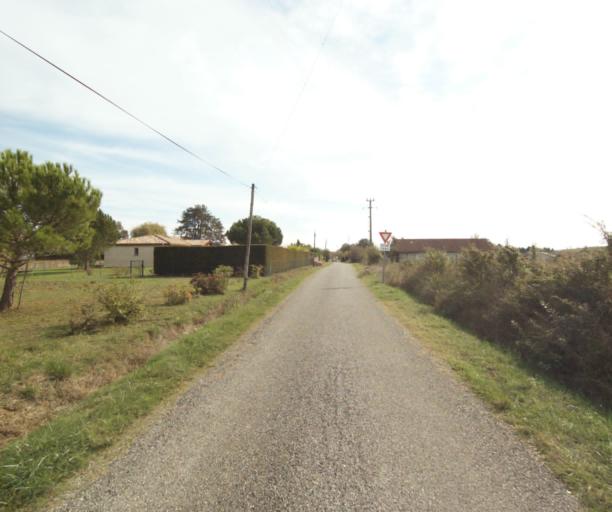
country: FR
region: Midi-Pyrenees
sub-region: Departement du Tarn-et-Garonne
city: Orgueil
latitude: 43.8947
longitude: 1.4041
